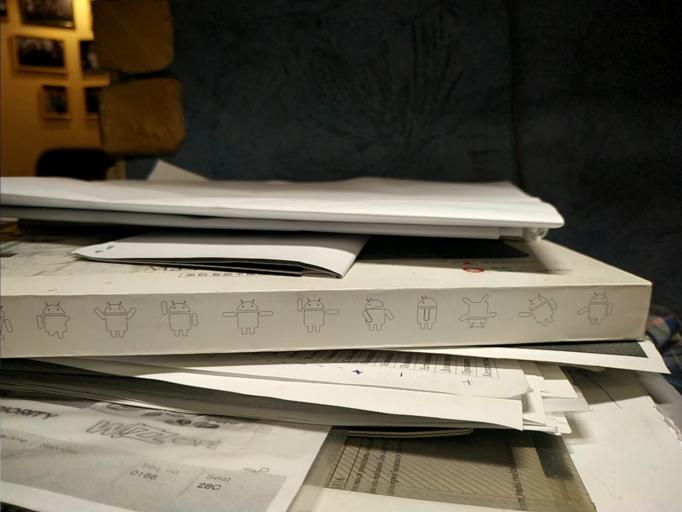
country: RU
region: Tverskaya
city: Zubtsov
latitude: 56.0842
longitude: 34.7798
